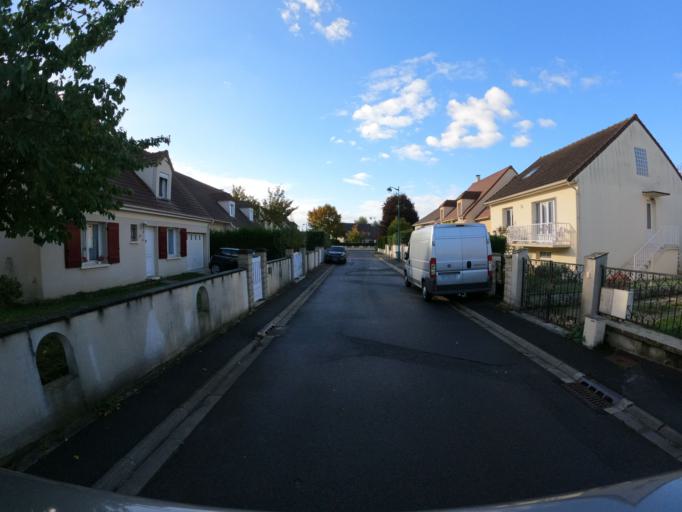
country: FR
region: Ile-de-France
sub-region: Departement de Seine-et-Marne
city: Bailly-Romainvilliers
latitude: 48.8487
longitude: 2.8270
